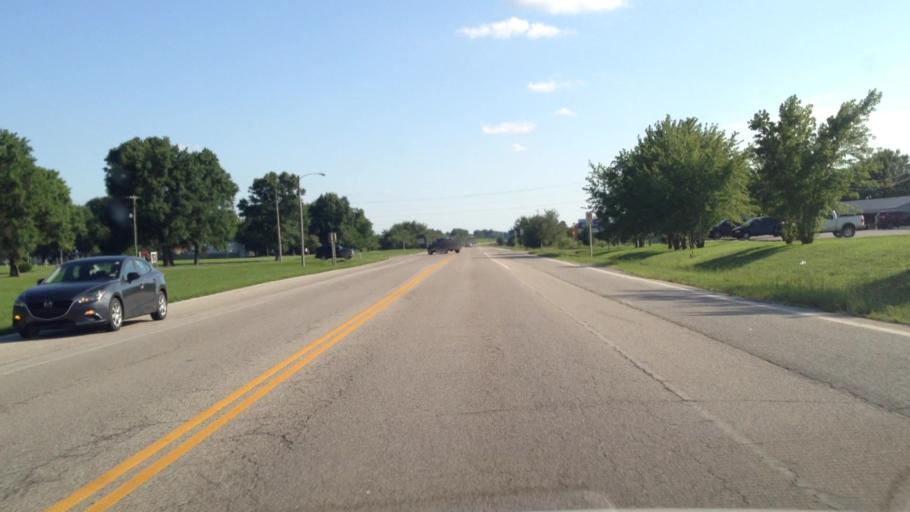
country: US
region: Kansas
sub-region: Crawford County
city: Arma
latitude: 37.5440
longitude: -94.7102
